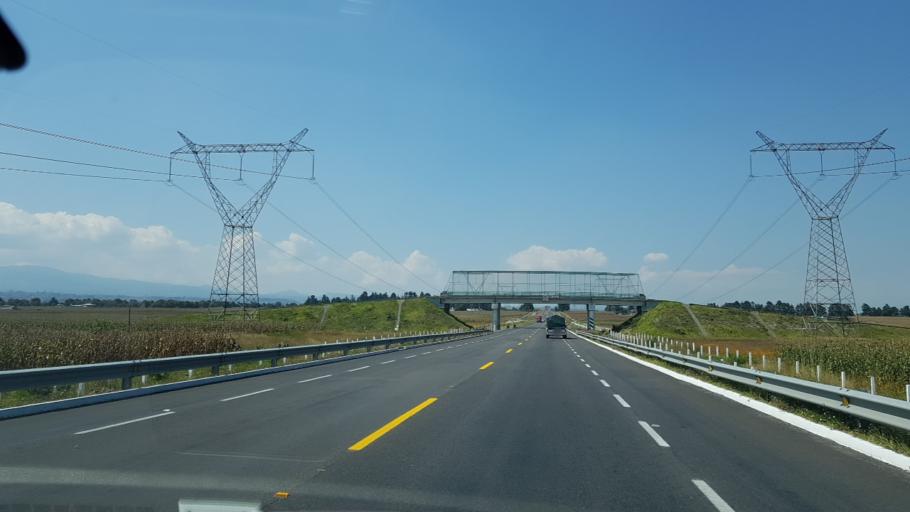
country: MX
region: Mexico
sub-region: Toluca
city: Sebastian Lerdo de Tejada
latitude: 19.3884
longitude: -99.7275
